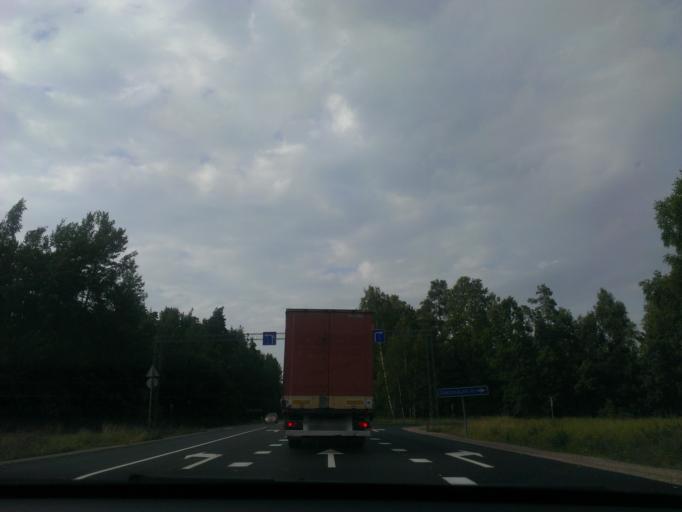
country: LV
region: Lecava
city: Iecava
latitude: 56.6619
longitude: 24.2327
